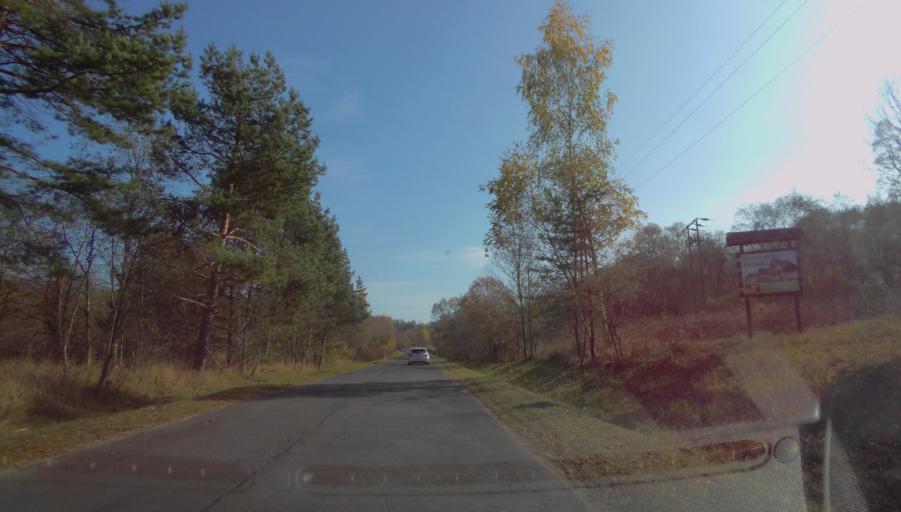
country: PL
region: Subcarpathian Voivodeship
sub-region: Powiat leski
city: Cisna
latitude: 49.2212
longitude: 22.1904
